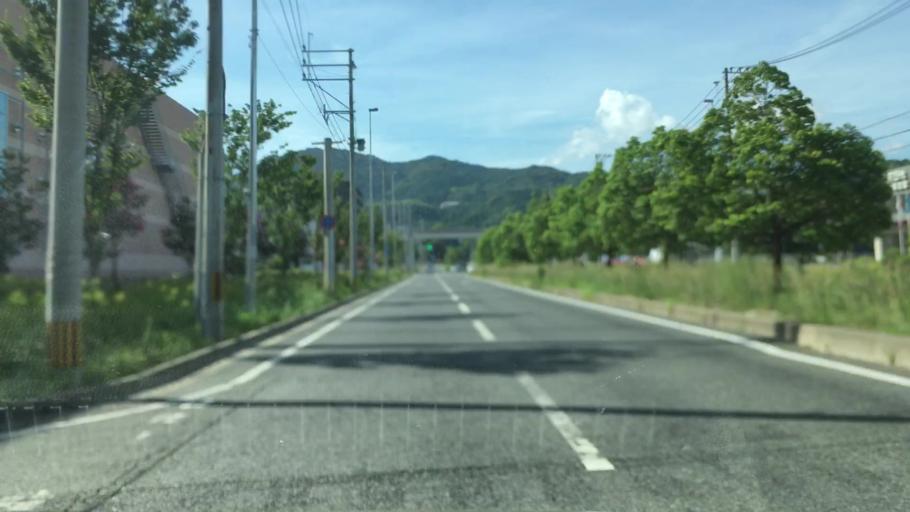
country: JP
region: Fukuoka
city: Maebaru-chuo
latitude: 33.5773
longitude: 130.2557
